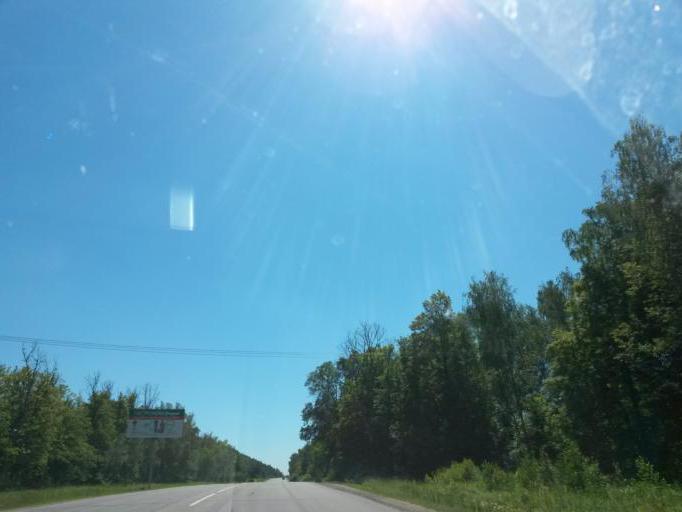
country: RU
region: Moskovskaya
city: Stolbovaya
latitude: 55.2007
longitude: 37.5066
